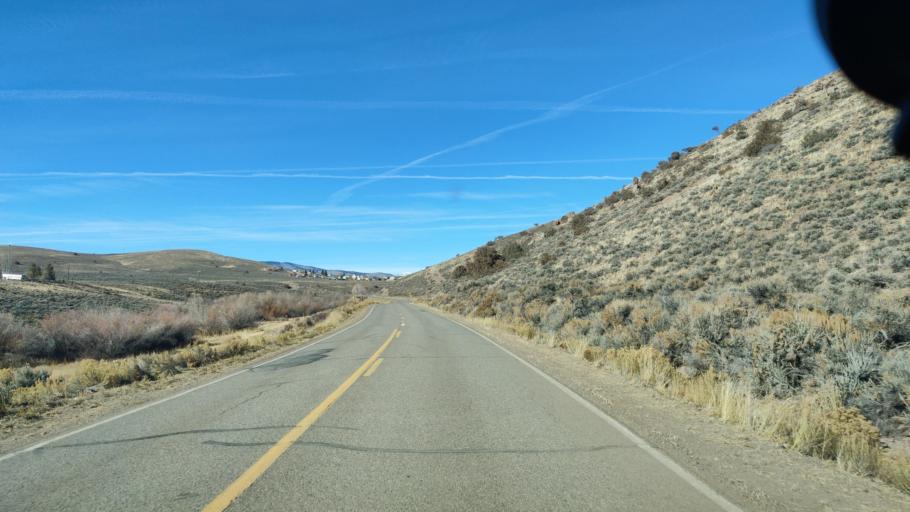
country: US
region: Colorado
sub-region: Gunnison County
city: Gunnison
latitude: 38.5652
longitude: -106.9575
